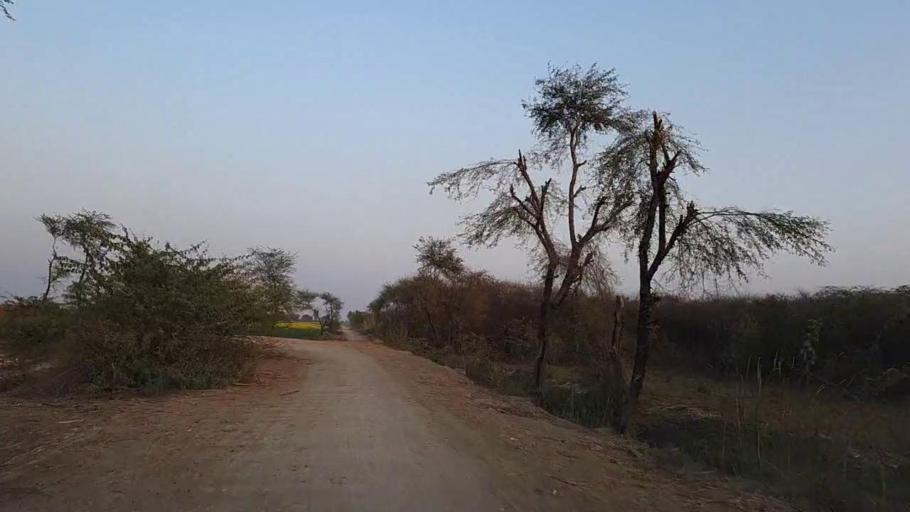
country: PK
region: Sindh
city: Jam Sahib
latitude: 26.3048
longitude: 68.5777
